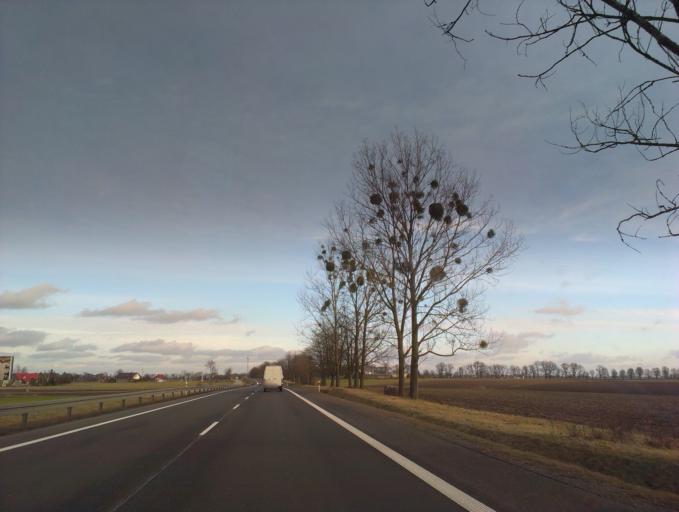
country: PL
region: Kujawsko-Pomorskie
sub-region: Powiat lipnowski
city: Kikol
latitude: 52.9324
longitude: 19.0442
